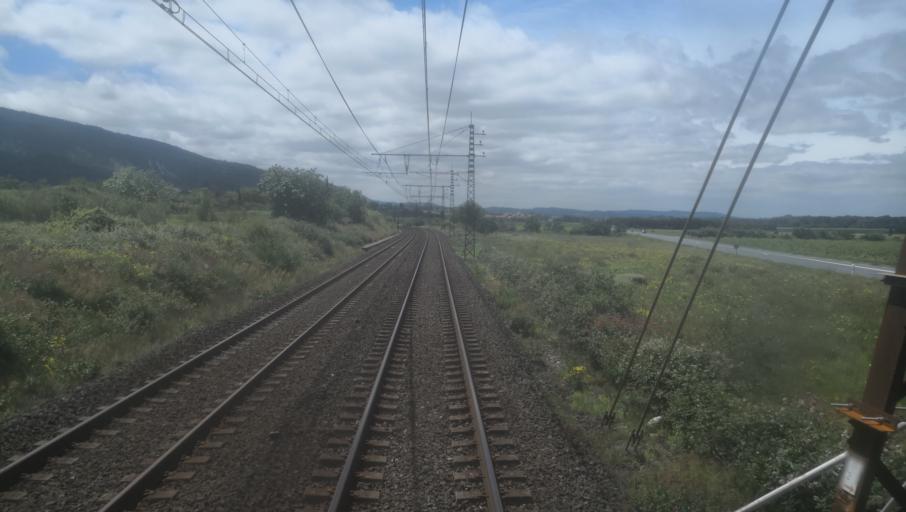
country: FR
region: Languedoc-Roussillon
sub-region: Departement de l'Aude
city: Capendu
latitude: 43.1864
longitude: 2.5393
